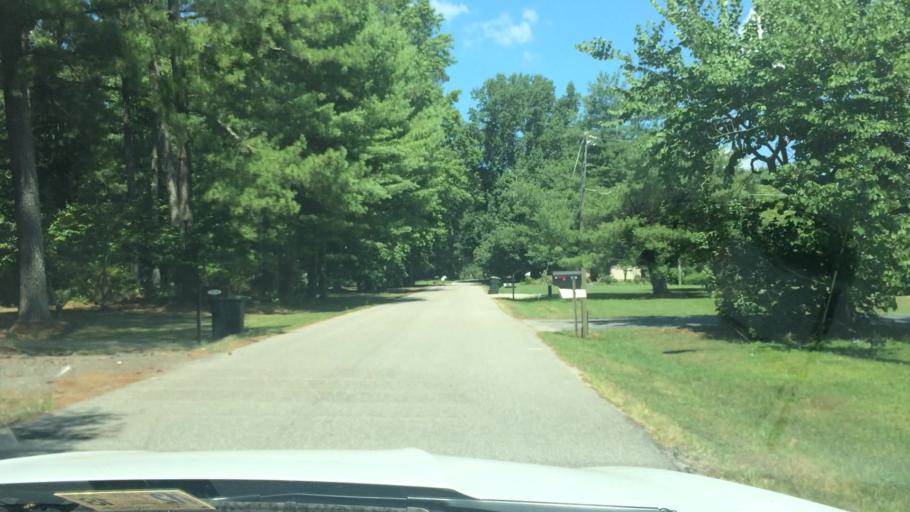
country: US
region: Virginia
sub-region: King William County
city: West Point
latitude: 37.5683
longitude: -76.8047
